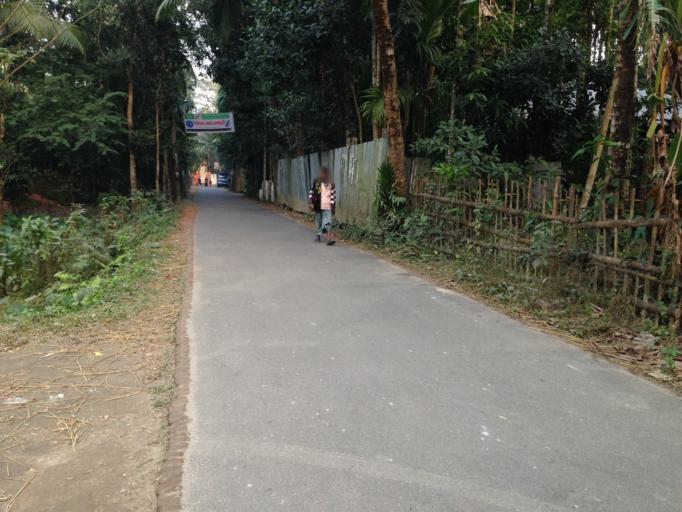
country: BD
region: Chittagong
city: Lakshmipur
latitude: 22.9204
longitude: 90.8389
